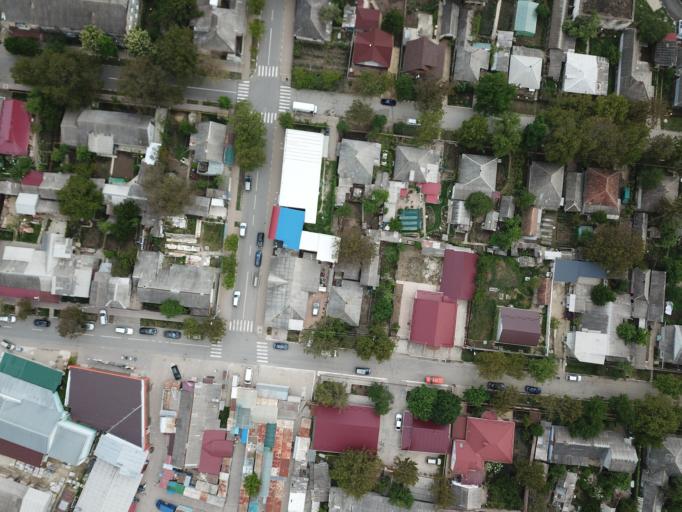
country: MD
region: Ungheni
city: Ungheni
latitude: 47.2100
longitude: 27.7949
